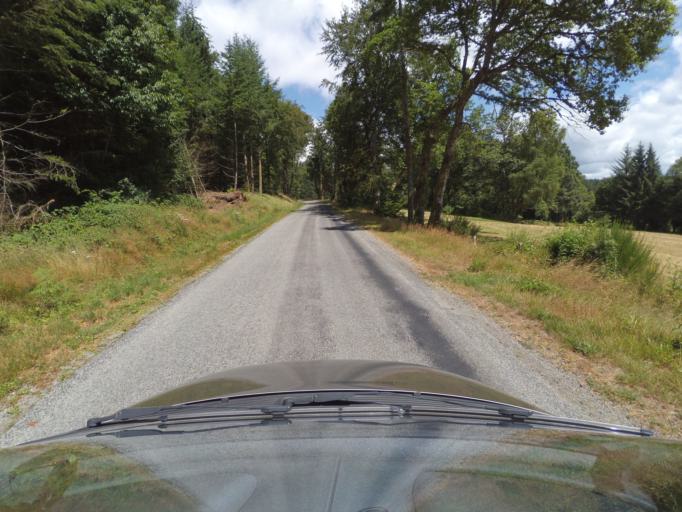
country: FR
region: Limousin
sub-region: Departement de la Creuse
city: Banize
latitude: 45.8018
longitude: 1.9313
